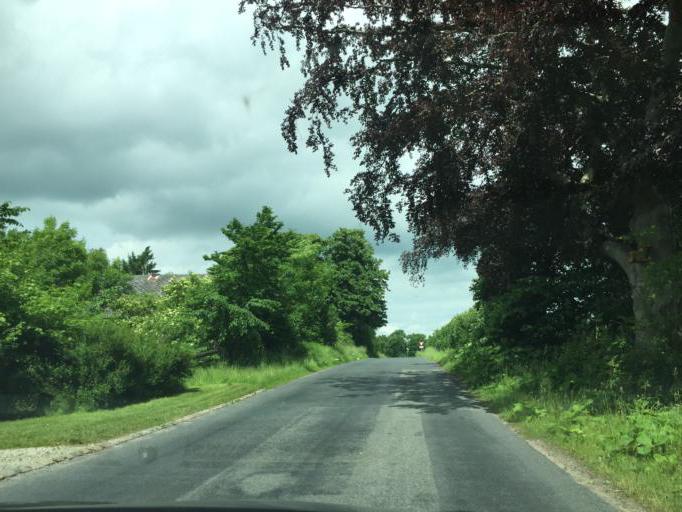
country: DK
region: South Denmark
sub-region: Faaborg-Midtfyn Kommune
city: Ringe
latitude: 55.2179
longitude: 10.4383
